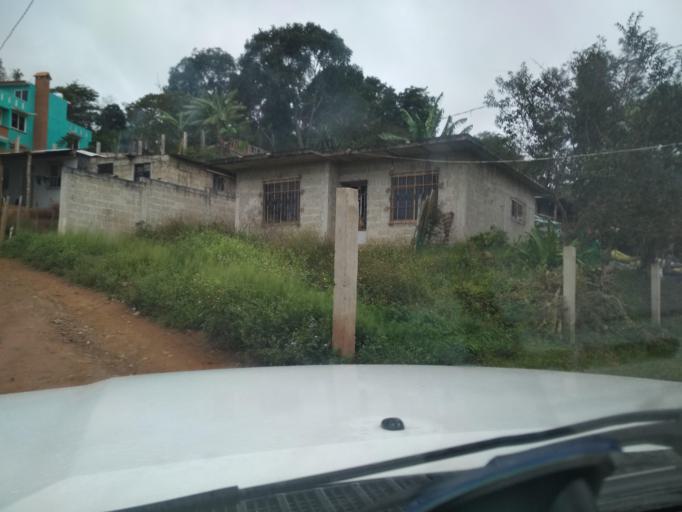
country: MX
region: Veracruz
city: El Castillo
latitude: 19.5392
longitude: -96.8294
